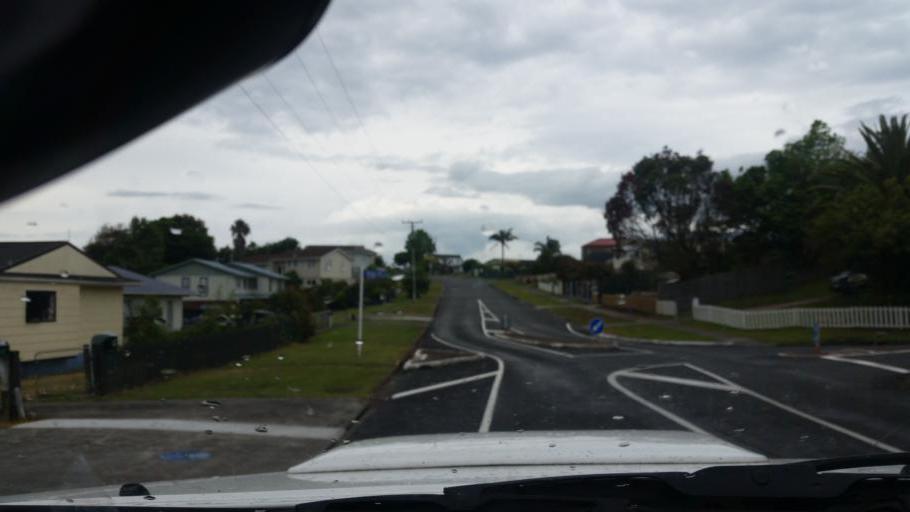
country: NZ
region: Northland
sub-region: Kaipara District
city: Dargaville
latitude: -35.9301
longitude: 173.8627
